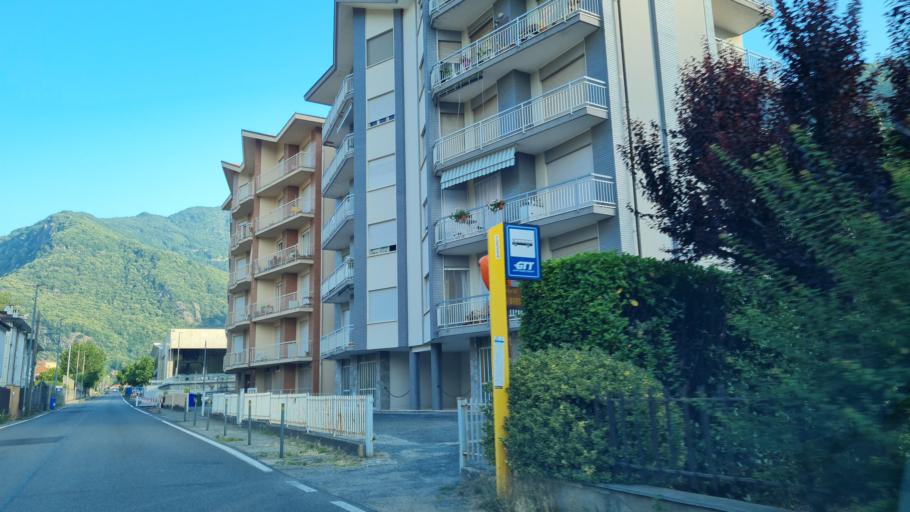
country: IT
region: Piedmont
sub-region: Provincia di Torino
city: Pont-Canavese
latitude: 45.4196
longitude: 7.6086
